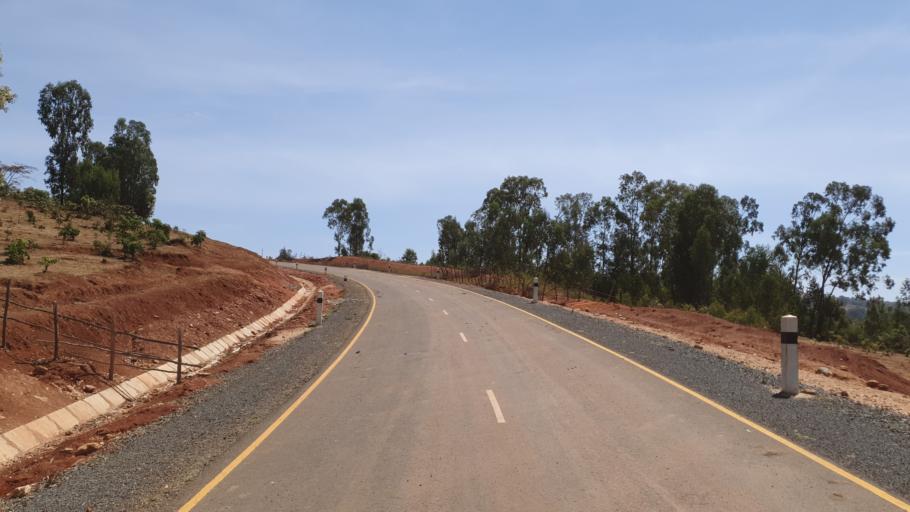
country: ET
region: Oromiya
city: Shambu
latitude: 9.8861
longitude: 36.6519
